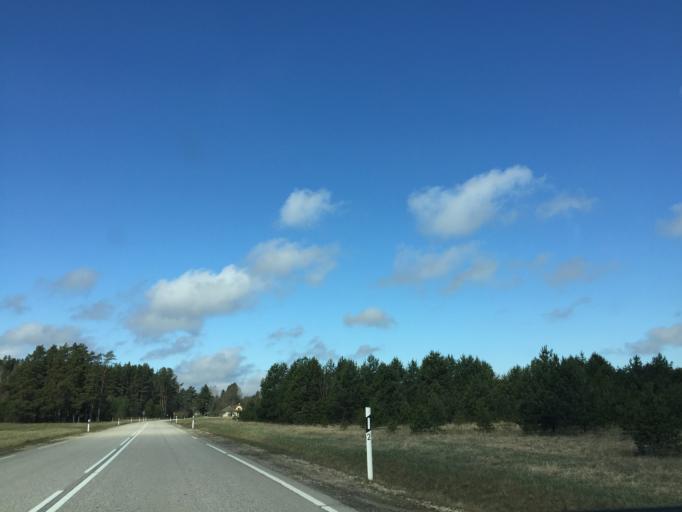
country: LV
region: Apes Novads
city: Ape
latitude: 57.5364
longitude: 26.7202
